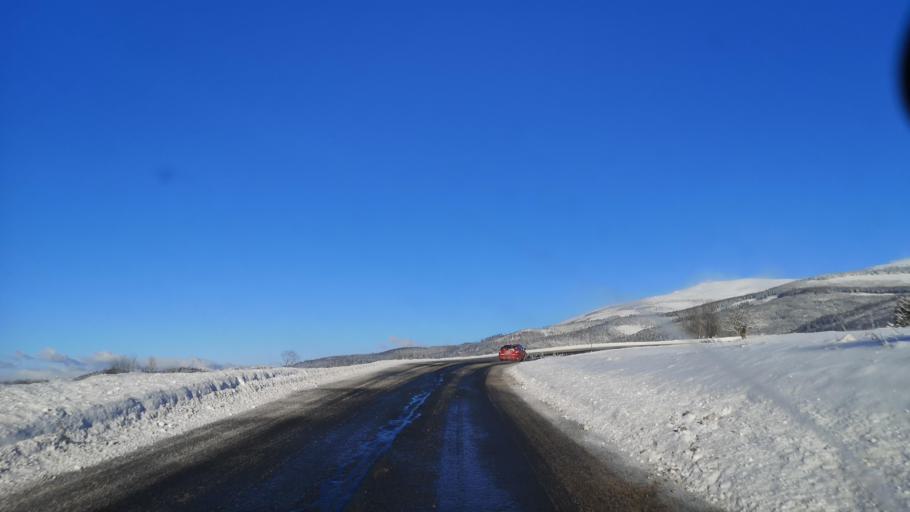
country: SK
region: Banskobystricky
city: Revuca
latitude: 48.8296
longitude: 20.1214
